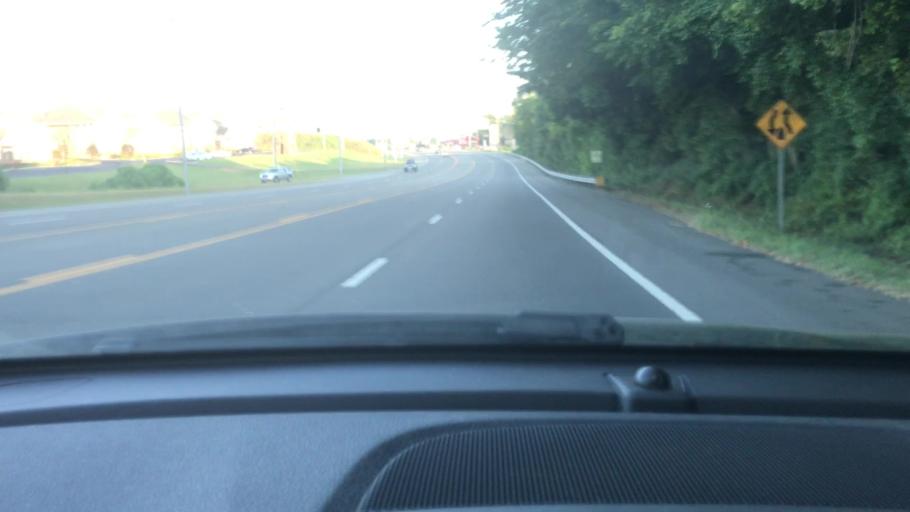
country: US
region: Tennessee
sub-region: Dickson County
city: Dickson
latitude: 36.0815
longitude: -87.3796
